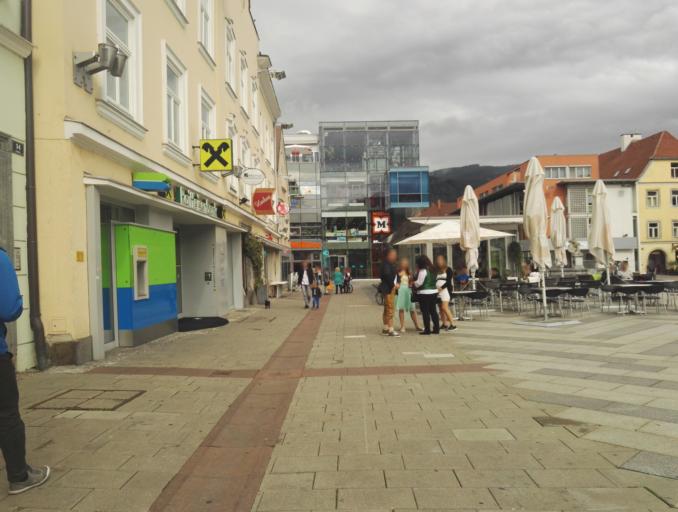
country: AT
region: Styria
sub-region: Politischer Bezirk Leoben
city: Leoben
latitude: 47.3808
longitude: 15.0945
